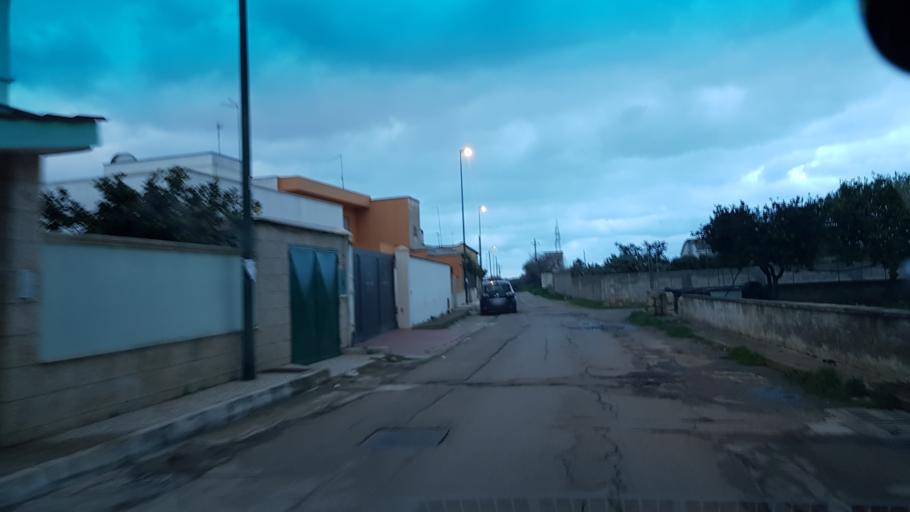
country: IT
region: Apulia
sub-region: Provincia di Brindisi
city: Torchiarolo
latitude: 40.4866
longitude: 18.0562
